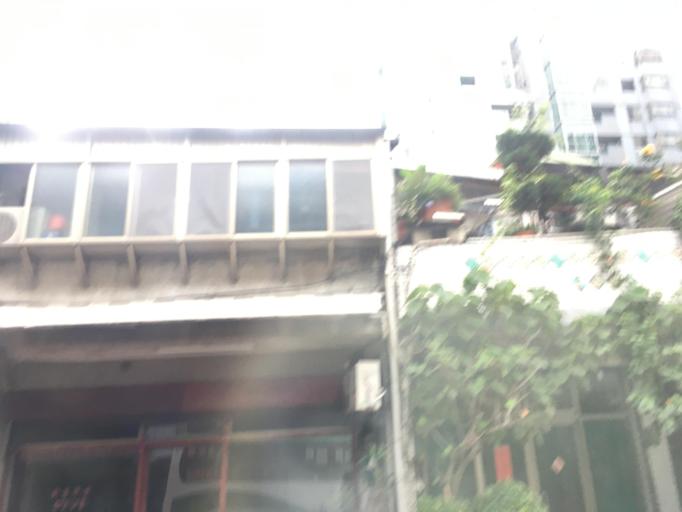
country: TW
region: Taipei
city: Taipei
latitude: 25.1262
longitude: 121.5280
